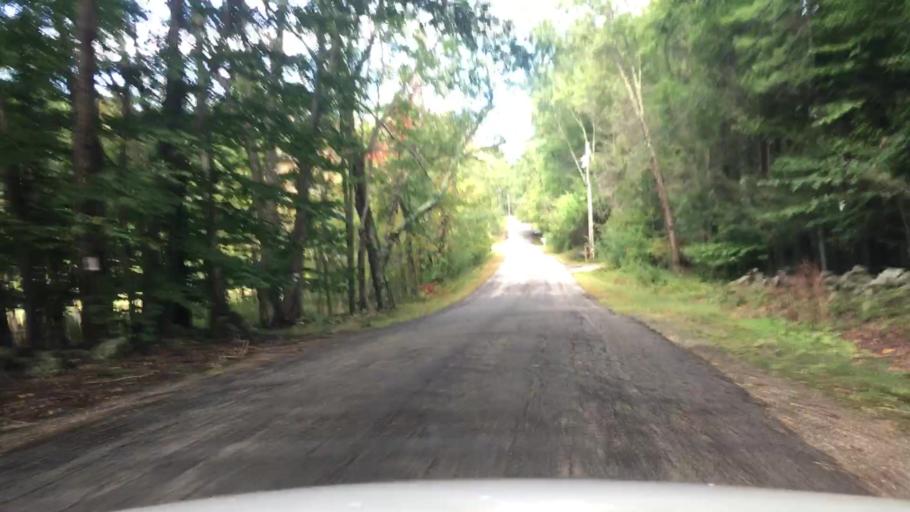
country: US
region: Maine
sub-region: York County
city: York Harbor
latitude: 43.1173
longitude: -70.6758
